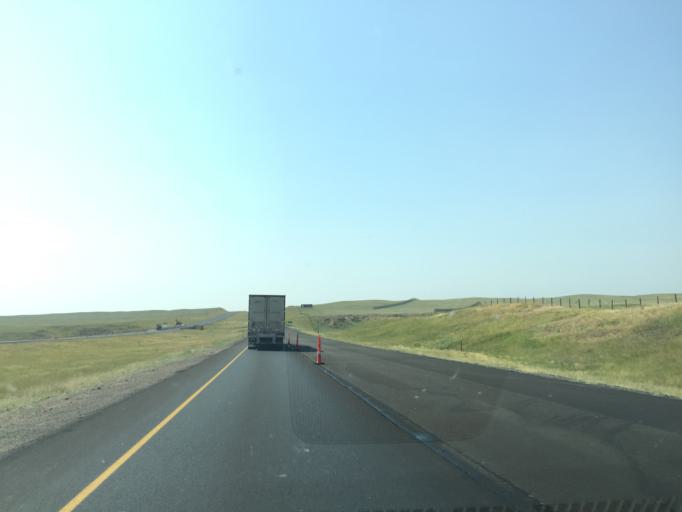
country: US
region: Wyoming
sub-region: Laramie County
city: Ranchettes
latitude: 41.3272
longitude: -104.8629
